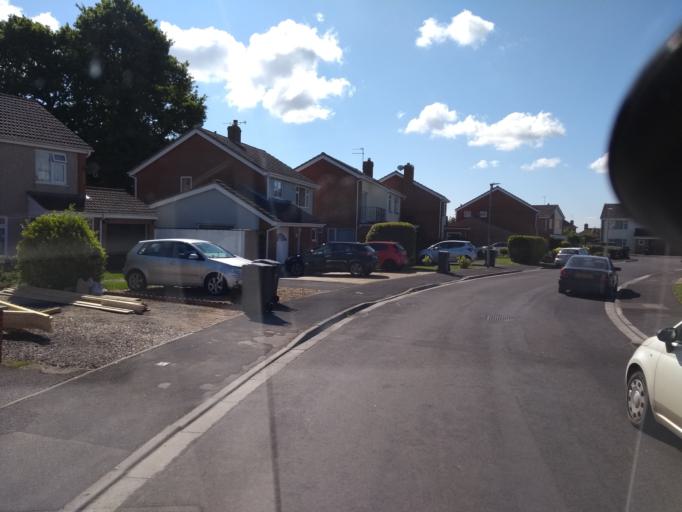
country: GB
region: England
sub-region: Somerset
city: Bridgwater
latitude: 51.1245
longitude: -3.0313
